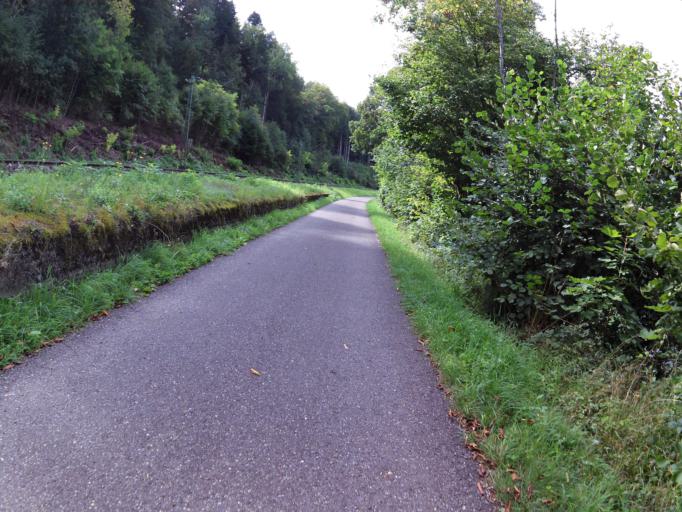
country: DE
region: Baden-Wuerttemberg
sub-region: Karlsruhe Region
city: Horb am Neckar
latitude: 48.4275
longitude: 8.6614
